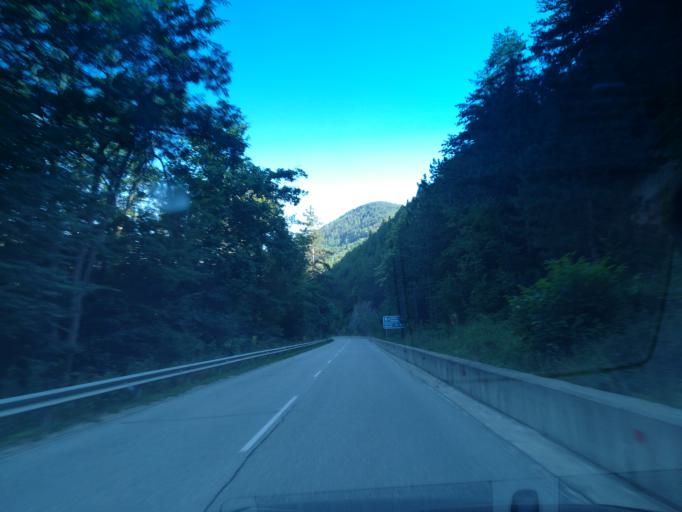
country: BG
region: Smolyan
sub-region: Obshtina Chepelare
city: Chepelare
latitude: 41.8344
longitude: 24.6836
